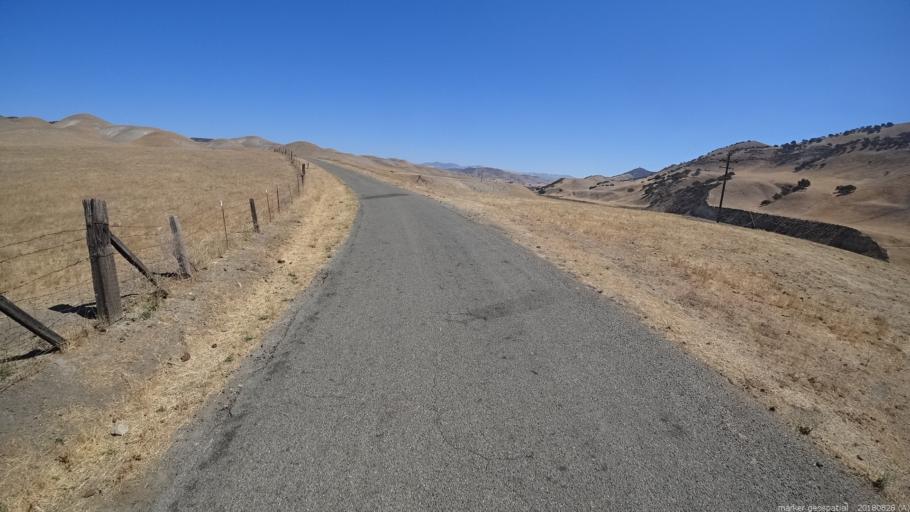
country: US
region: California
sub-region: San Luis Obispo County
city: San Miguel
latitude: 36.0519
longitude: -120.8135
